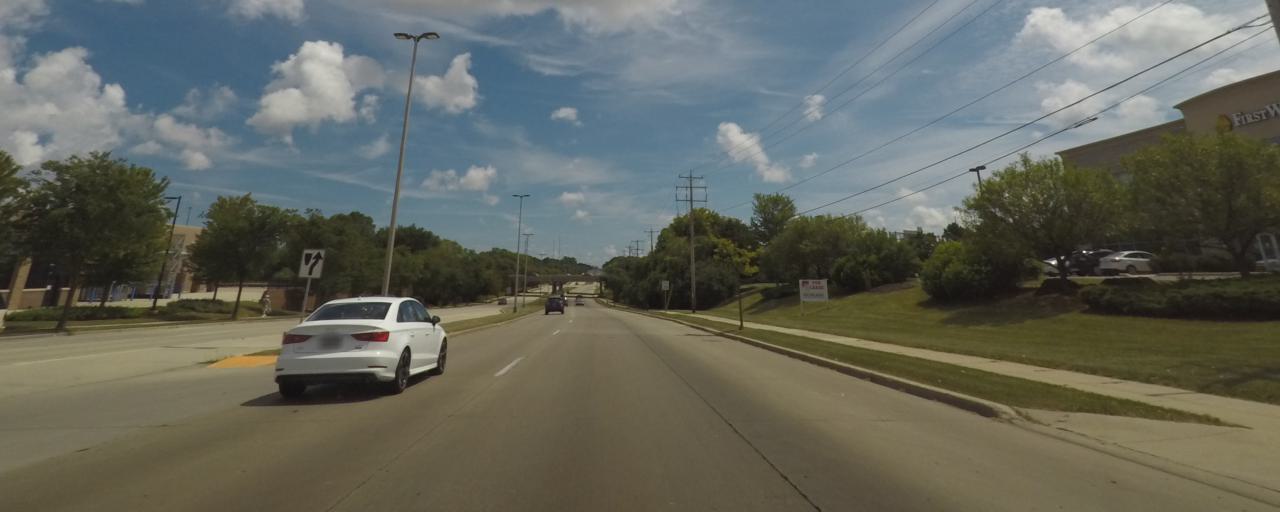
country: US
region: Wisconsin
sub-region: Milwaukee County
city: Hales Corners
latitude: 42.9591
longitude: -88.0450
